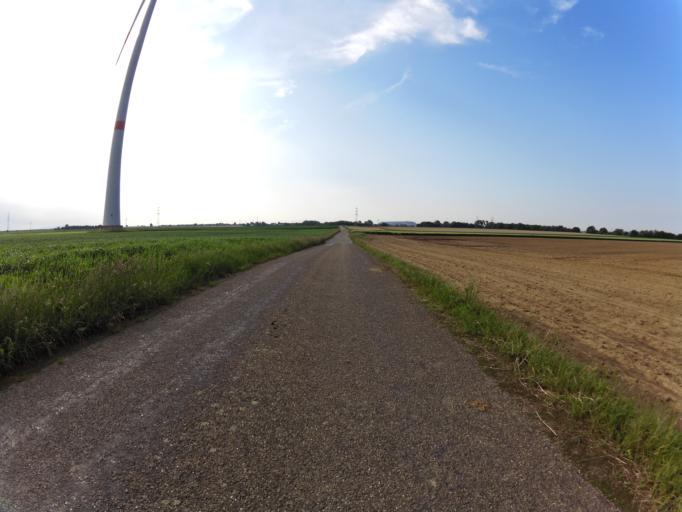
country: DE
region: North Rhine-Westphalia
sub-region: Regierungsbezirk Koln
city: Linnich
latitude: 50.9742
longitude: 6.2068
